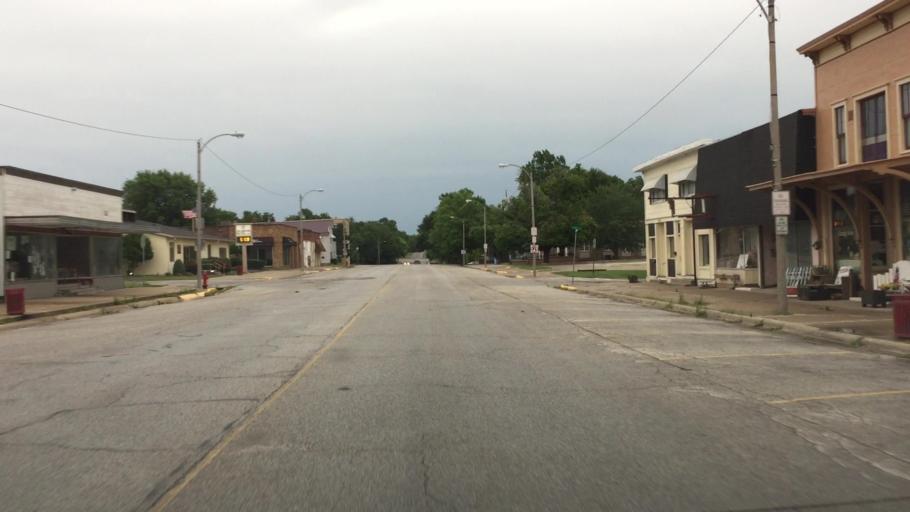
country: US
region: Illinois
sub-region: Hancock County
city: Hamilton
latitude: 40.3931
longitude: -91.3445
